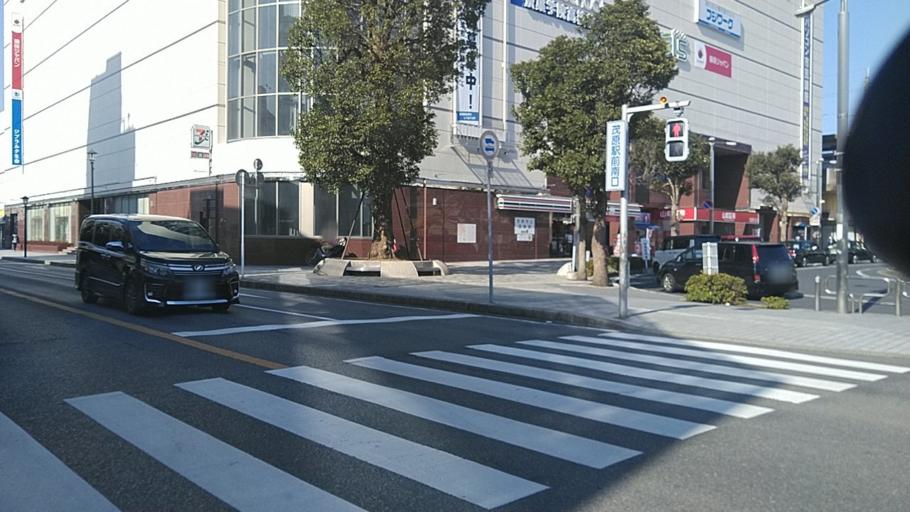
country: JP
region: Chiba
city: Mobara
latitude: 35.4263
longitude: 140.3034
